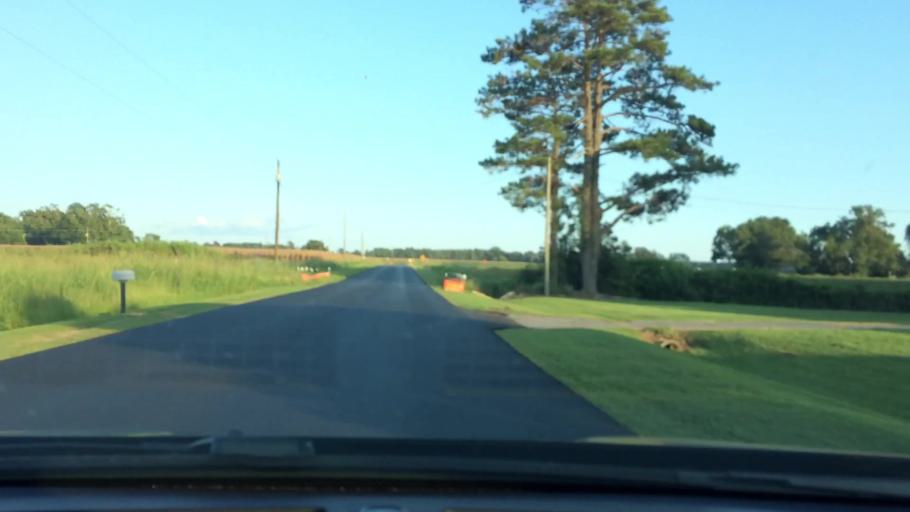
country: US
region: North Carolina
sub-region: Pitt County
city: Ayden
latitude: 35.4449
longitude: -77.4574
